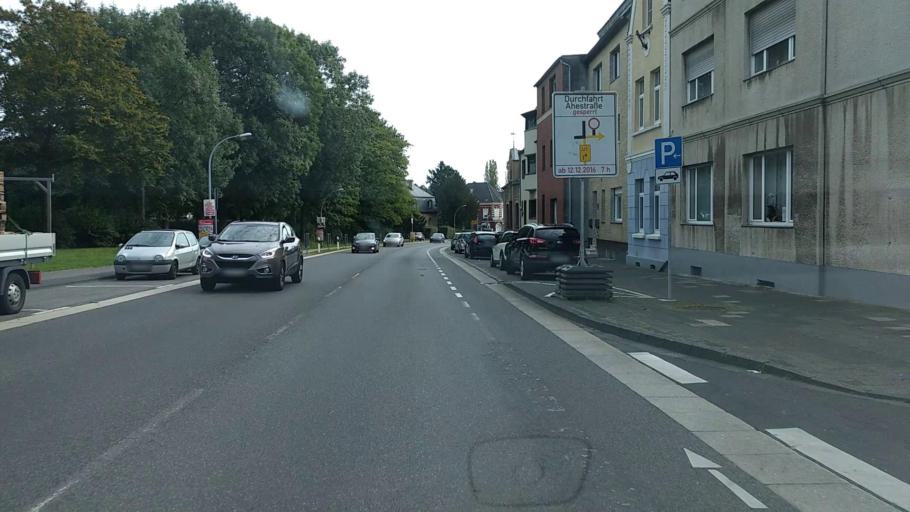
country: DE
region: North Rhine-Westphalia
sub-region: Regierungsbezirk Koln
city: Bergheim
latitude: 50.9427
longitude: 6.6775
